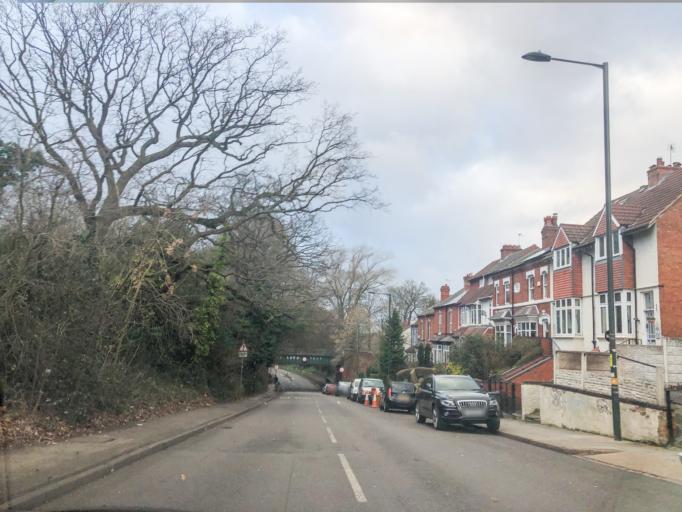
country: GB
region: England
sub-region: City and Borough of Birmingham
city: Birmingham
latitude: 52.4341
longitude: -1.9015
